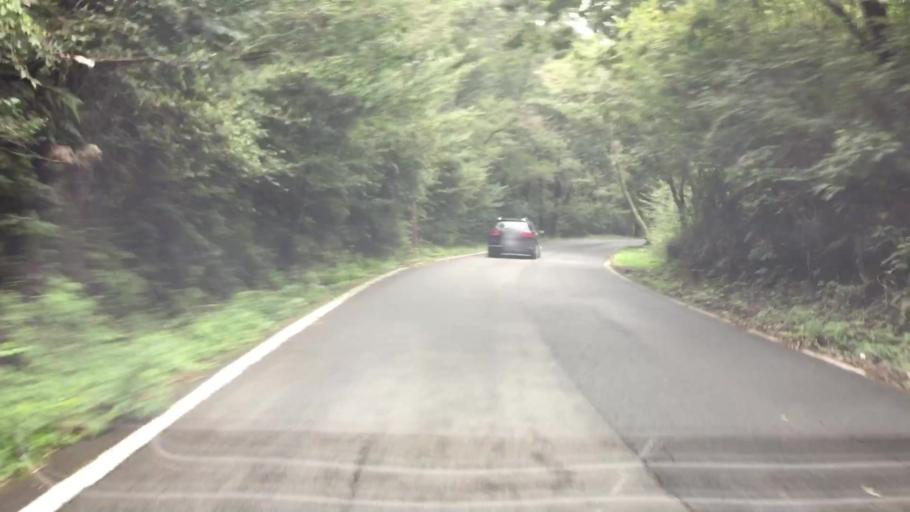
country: JP
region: Shizuoka
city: Fujinomiya
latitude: 35.3656
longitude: 138.5887
